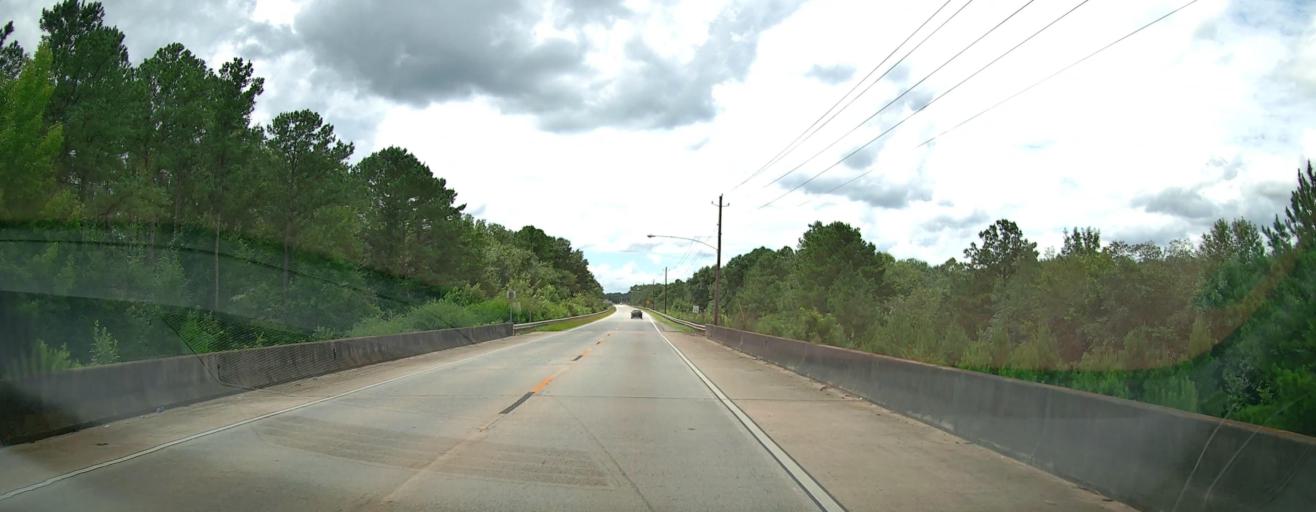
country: US
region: Georgia
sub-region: Macon County
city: Montezuma
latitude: 32.2932
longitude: -84.0365
